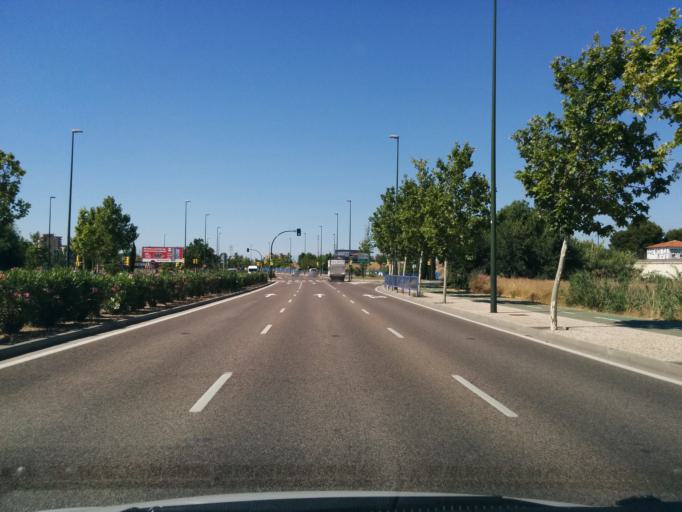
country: ES
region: Aragon
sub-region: Provincia de Zaragoza
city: Zaragoza
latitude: 41.6556
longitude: -0.8534
